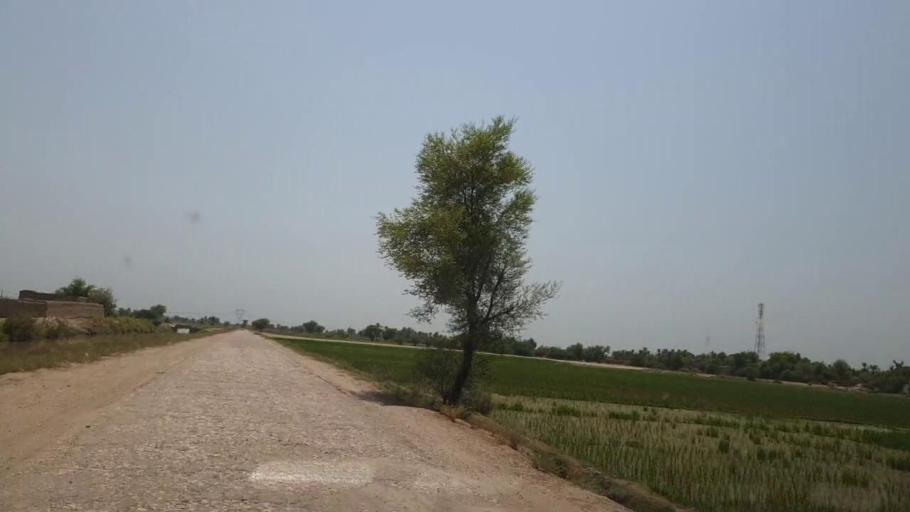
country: PK
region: Sindh
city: Lakhi
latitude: 27.8630
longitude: 68.6060
